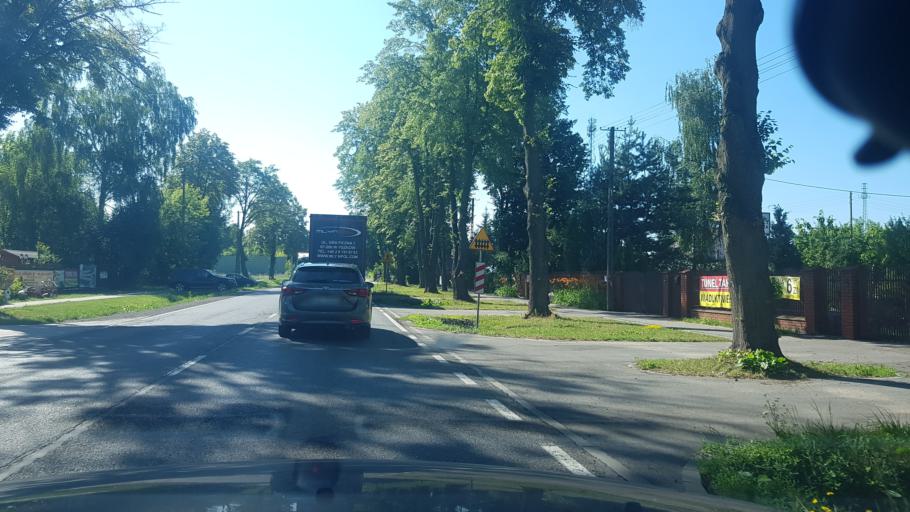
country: PL
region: Masovian Voivodeship
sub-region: Powiat wegrowski
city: Lochow
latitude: 52.5320
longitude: 21.6790
